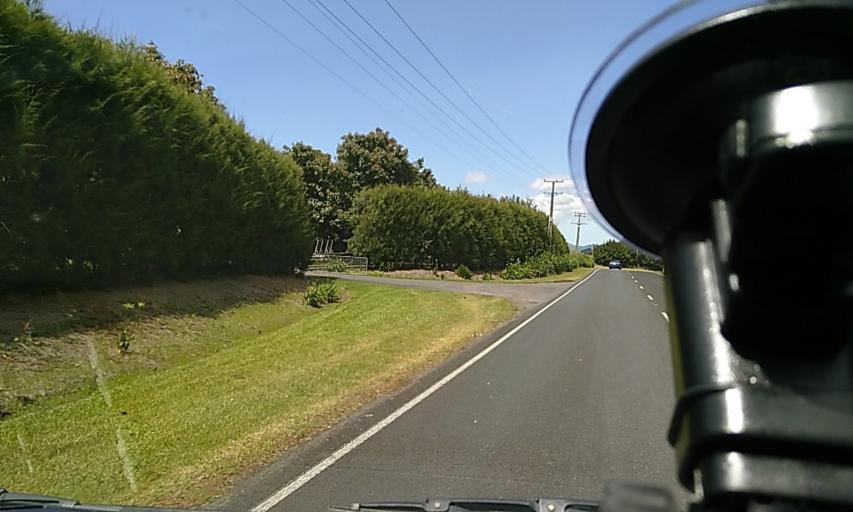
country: NZ
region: Bay of Plenty
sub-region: Western Bay of Plenty District
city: Waihi Beach
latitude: -37.4540
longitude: 175.9418
